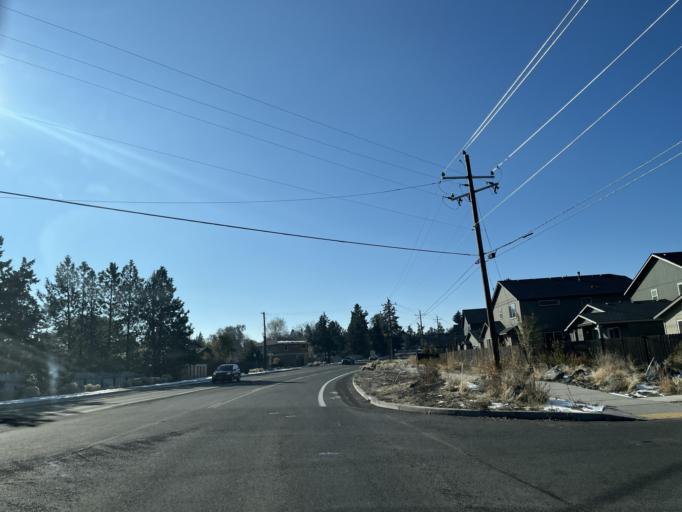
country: US
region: Oregon
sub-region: Deschutes County
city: Bend
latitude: 44.0788
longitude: -121.2834
